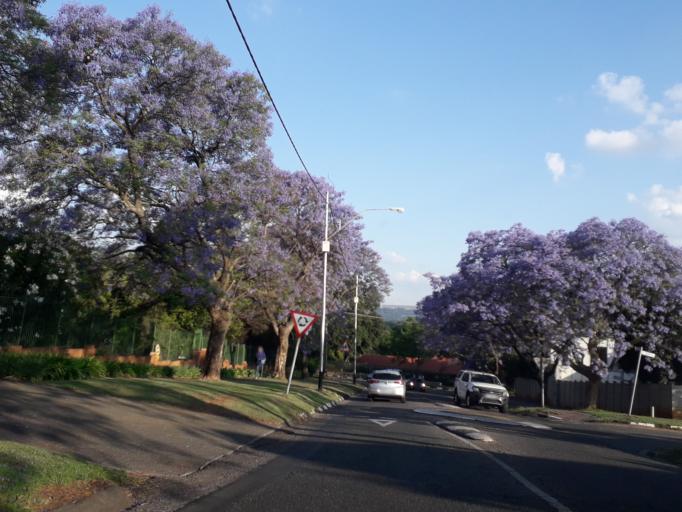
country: ZA
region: Gauteng
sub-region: City of Johannesburg Metropolitan Municipality
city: Johannesburg
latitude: -26.1373
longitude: 28.0019
